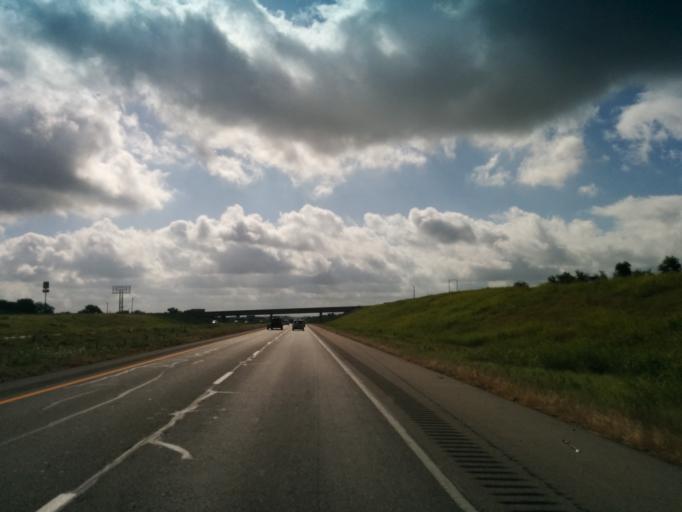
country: US
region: Texas
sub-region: Caldwell County
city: Luling
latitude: 29.6513
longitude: -97.6638
